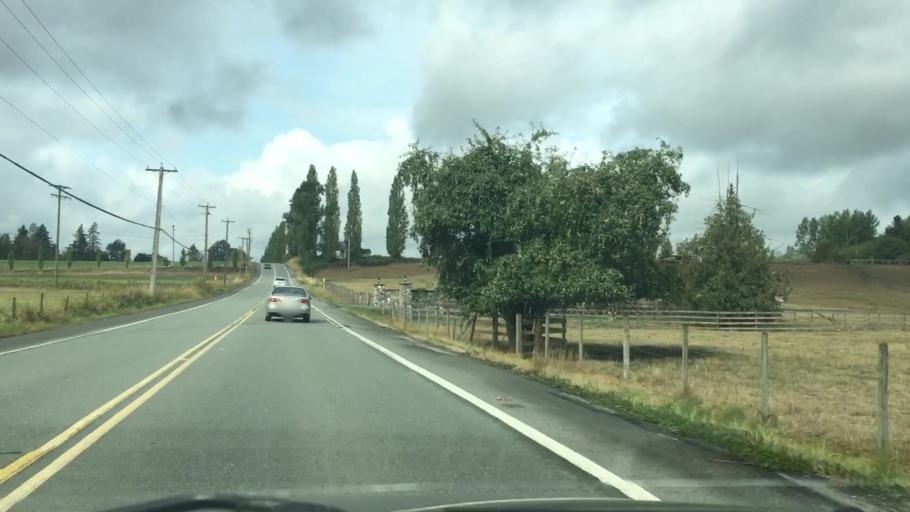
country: CA
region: British Columbia
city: Langley
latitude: 49.1043
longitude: -122.5893
